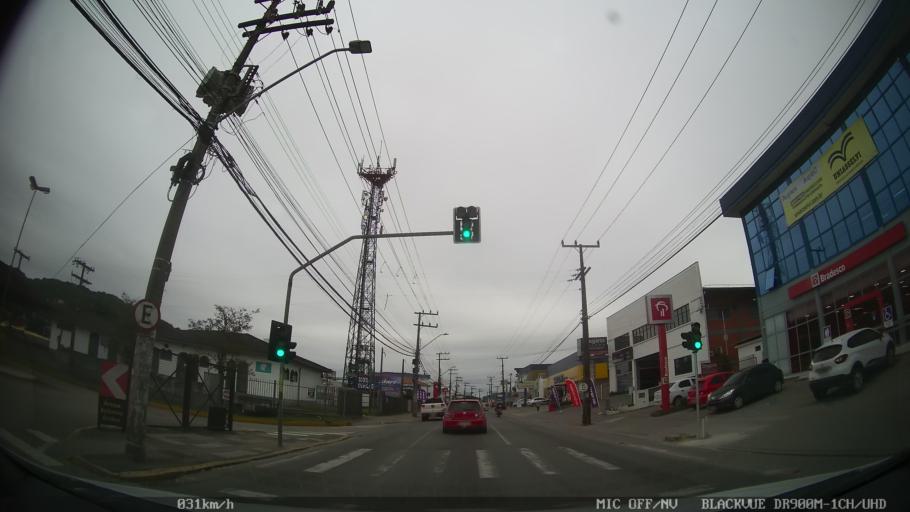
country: BR
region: Santa Catarina
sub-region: Joinville
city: Joinville
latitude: -26.2723
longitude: -48.8286
